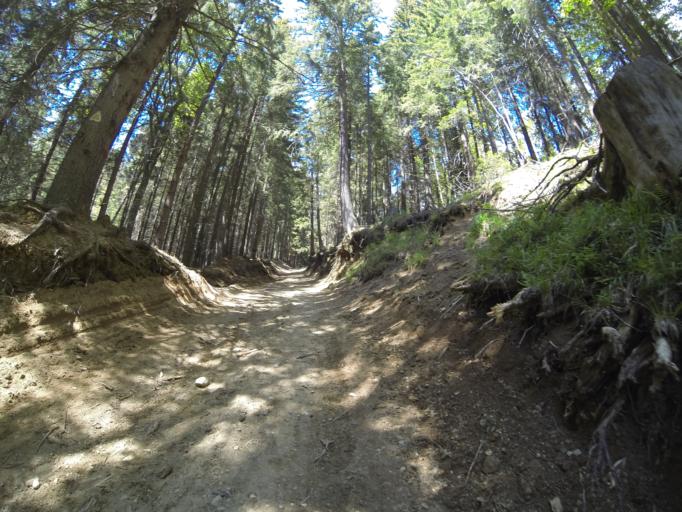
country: RO
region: Brasov
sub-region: Comuna Zarnesti
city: Zarnesti
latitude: 45.5416
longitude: 25.2524
